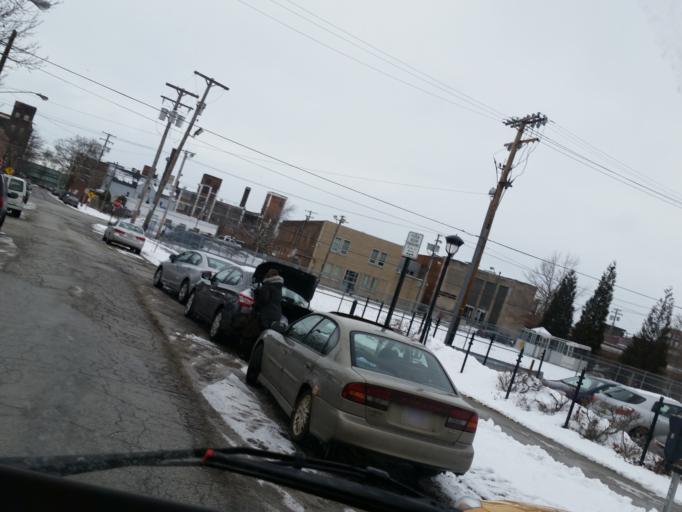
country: US
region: Ohio
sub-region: Cuyahoga County
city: Cleveland
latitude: 41.5052
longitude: -81.6753
